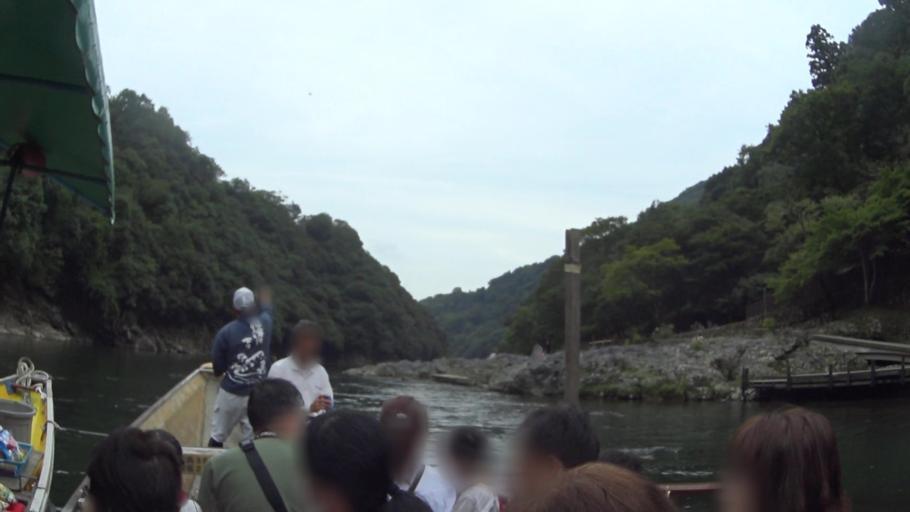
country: JP
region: Kyoto
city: Muko
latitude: 35.0163
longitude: 135.6679
